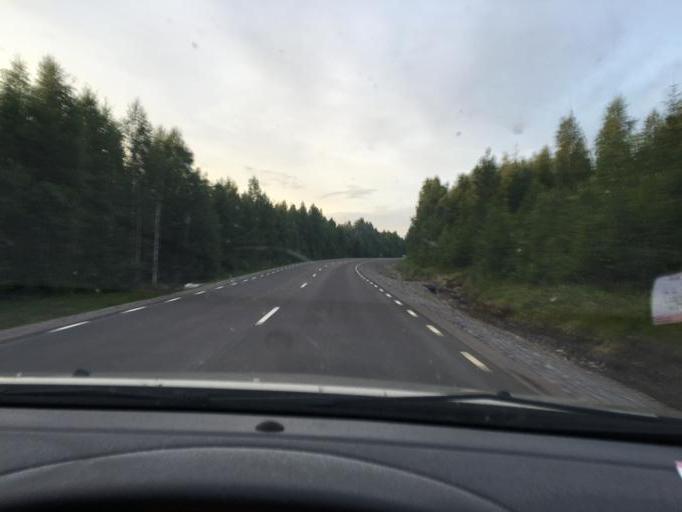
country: SE
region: Norrbotten
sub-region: Lulea Kommun
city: Ranea
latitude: 66.0485
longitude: 22.2063
